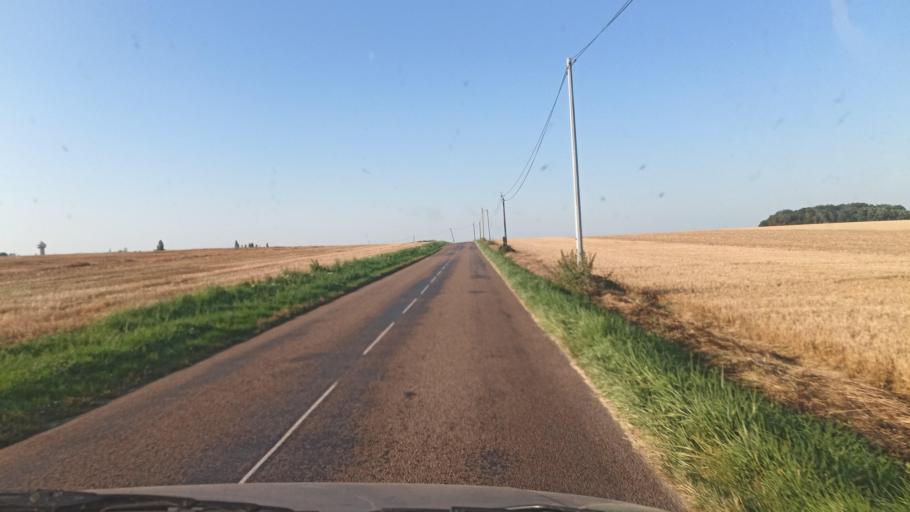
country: FR
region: Bourgogne
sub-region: Departement de l'Yonne
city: Saint-Valerien
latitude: 48.2008
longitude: 3.1174
